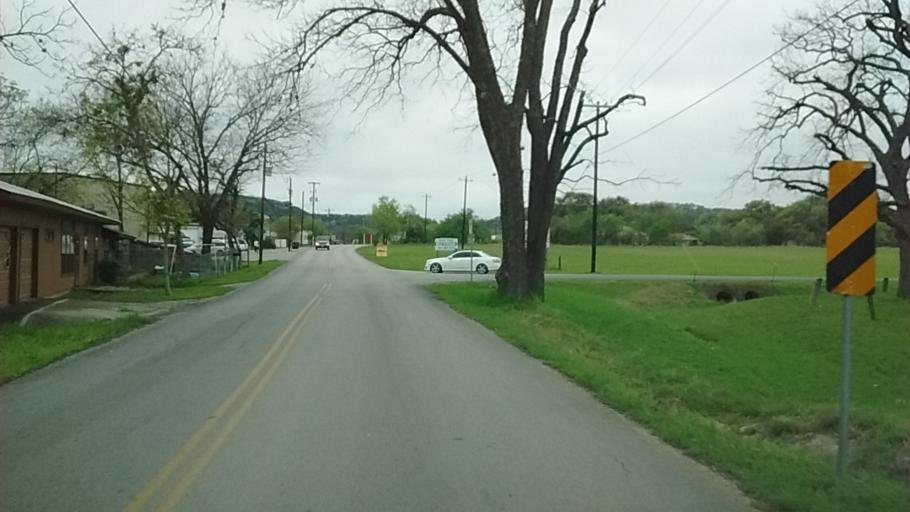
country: US
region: Texas
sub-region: Comal County
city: Canyon Lake
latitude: 29.8452
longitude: -98.1703
